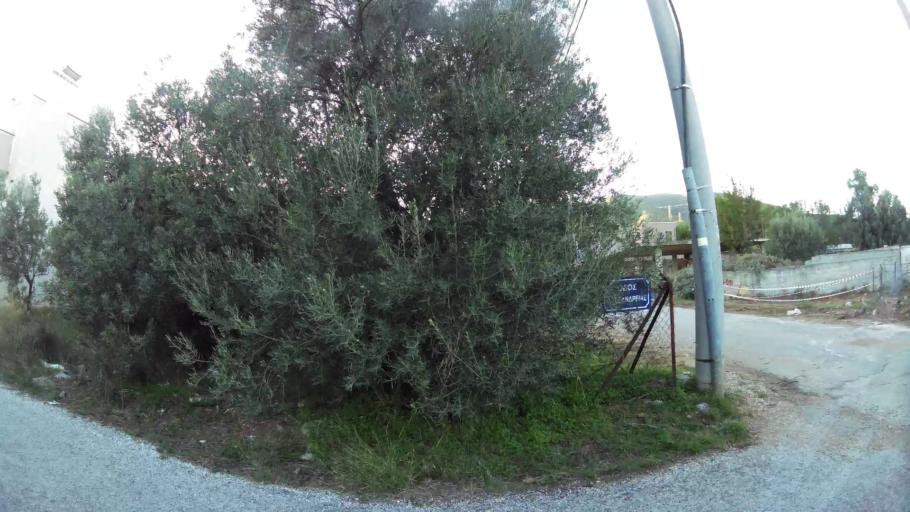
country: GR
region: Attica
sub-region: Nomarchia Anatolikis Attikis
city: Paiania
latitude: 37.9699
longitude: 23.8487
